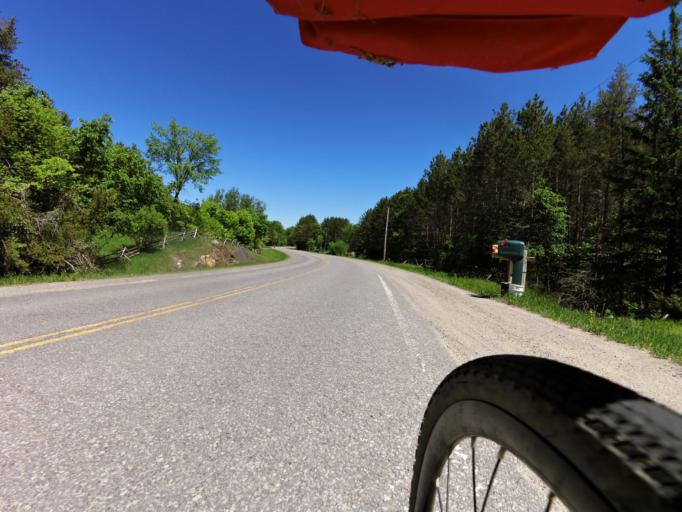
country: CA
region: Ontario
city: Carleton Place
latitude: 45.1835
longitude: -76.3626
